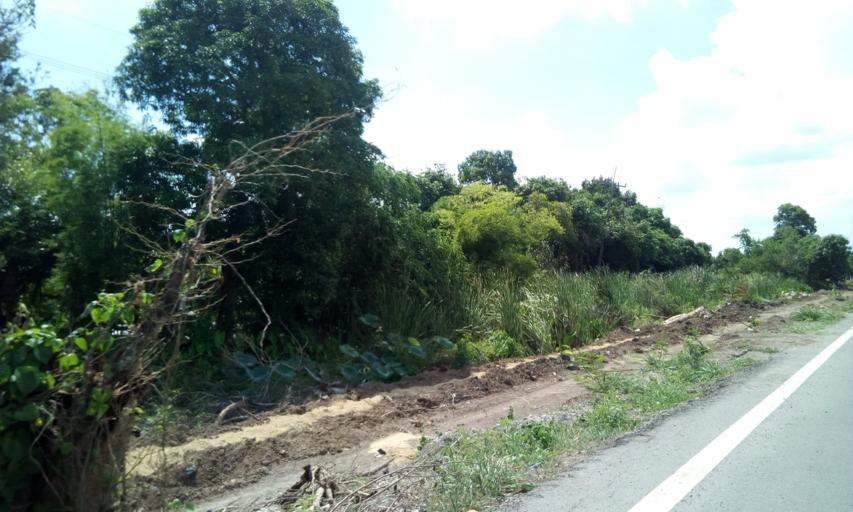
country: TH
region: Nakhon Nayok
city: Ongkharak
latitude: 14.0871
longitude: 100.9144
